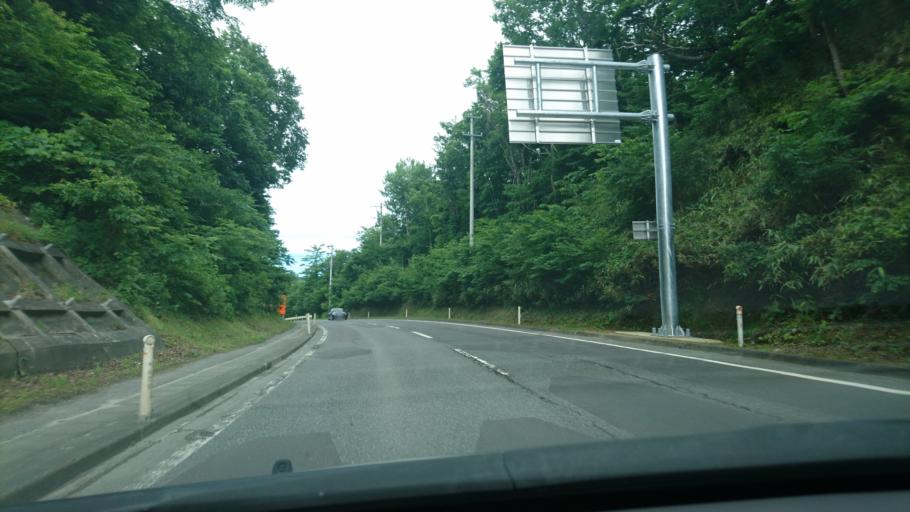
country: JP
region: Iwate
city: Miyako
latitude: 39.9498
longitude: 141.8419
